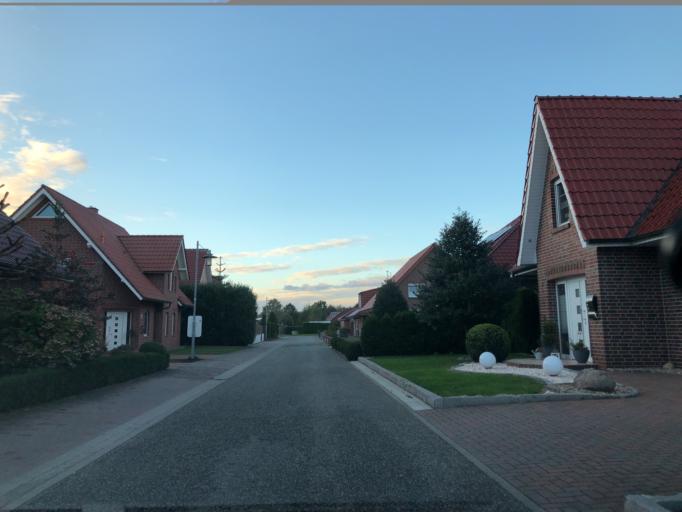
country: DE
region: Lower Saxony
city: Papenburg
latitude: 53.0860
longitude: 7.4217
